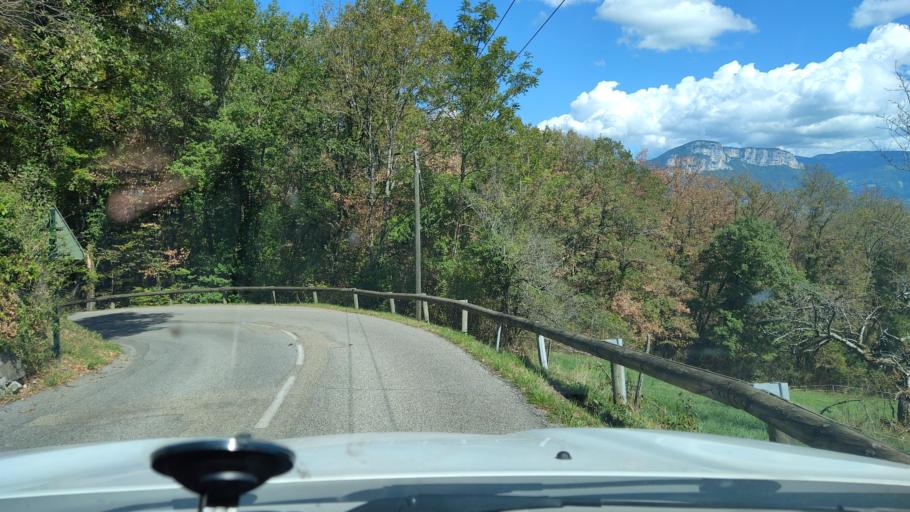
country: FR
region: Rhone-Alpes
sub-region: Departement de la Savoie
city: Jacob-Bellecombette
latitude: 45.5426
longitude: 5.9138
